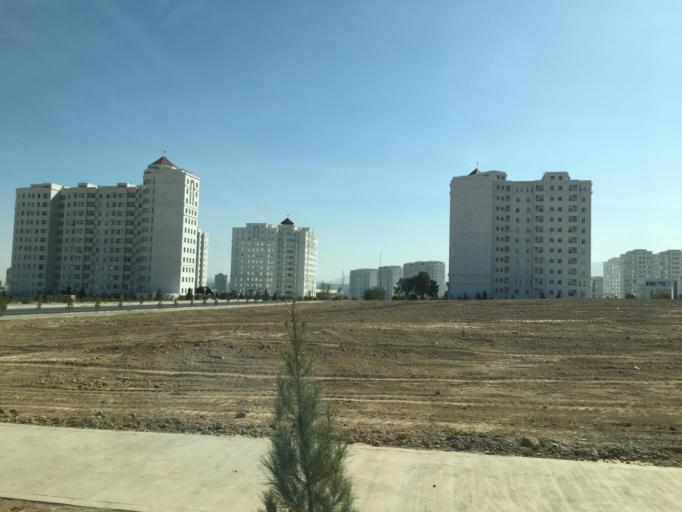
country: TM
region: Ahal
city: Ashgabat
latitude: 37.9260
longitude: 58.3625
